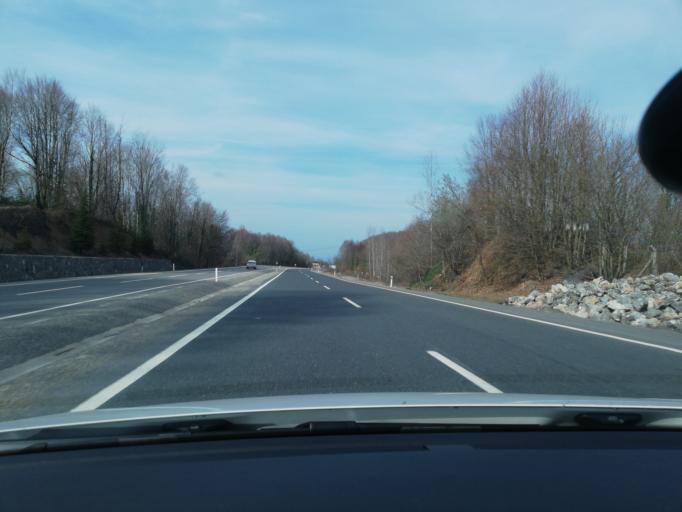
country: TR
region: Zonguldak
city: Kozlu
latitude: 41.3345
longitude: 31.6278
